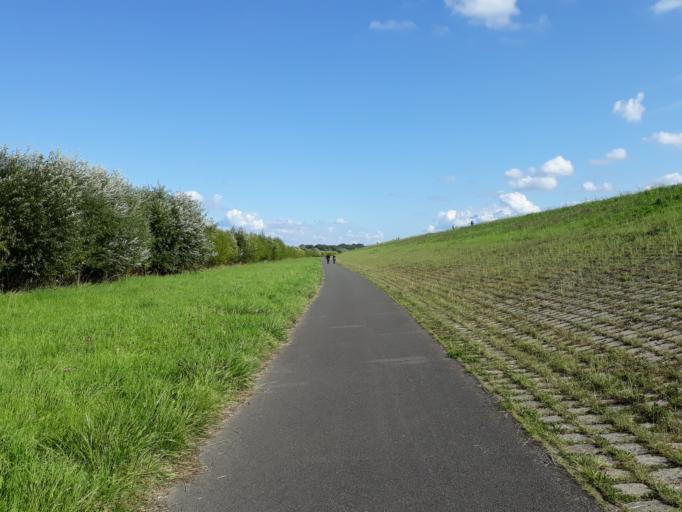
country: DE
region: Lower Saxony
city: Grunendeich
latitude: 53.5693
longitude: 9.6407
